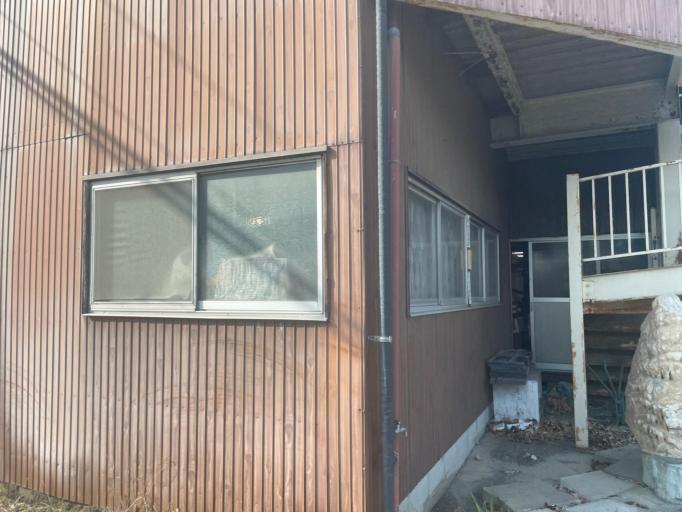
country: JP
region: Tochigi
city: Ashikaga
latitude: 36.3189
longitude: 139.4924
